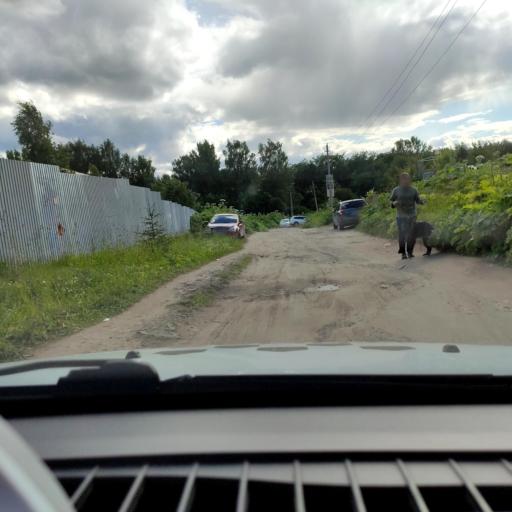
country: RU
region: Perm
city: Overyata
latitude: 58.0995
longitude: 55.8579
